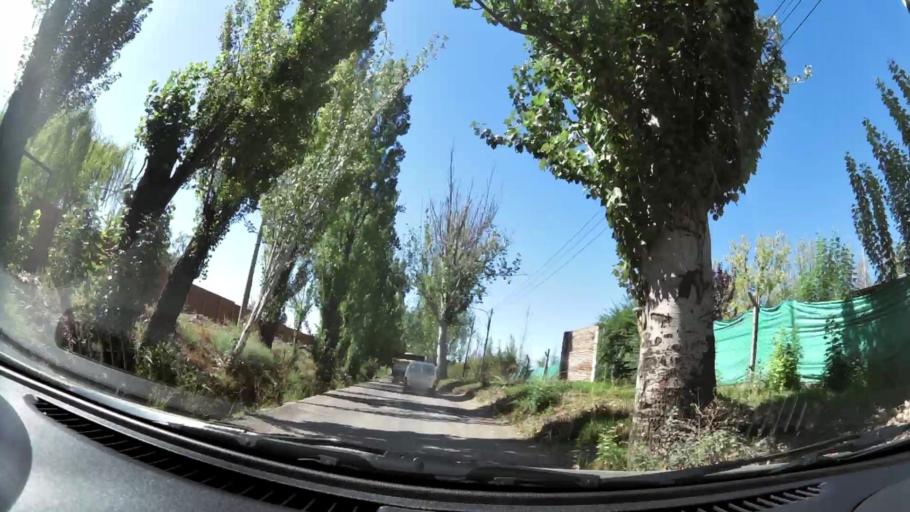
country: AR
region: Mendoza
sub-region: Departamento de Godoy Cruz
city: Godoy Cruz
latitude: -32.9772
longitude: -68.8411
